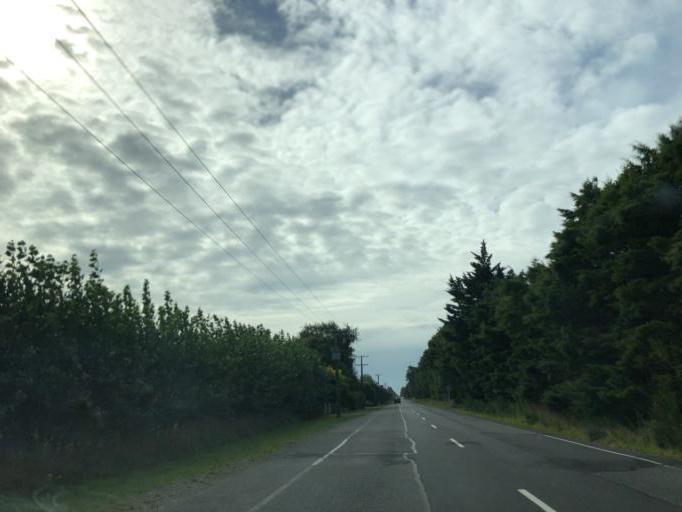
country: NZ
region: Canterbury
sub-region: Selwyn District
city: Rolleston
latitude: -43.6211
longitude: 172.4039
